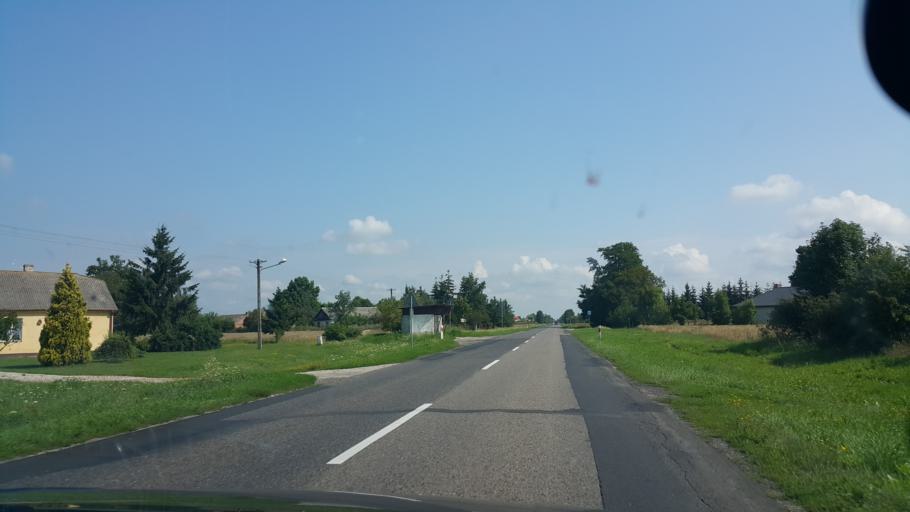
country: PL
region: Lublin Voivodeship
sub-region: Powiat wlodawski
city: Urszulin
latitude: 51.3749
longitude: 23.1839
